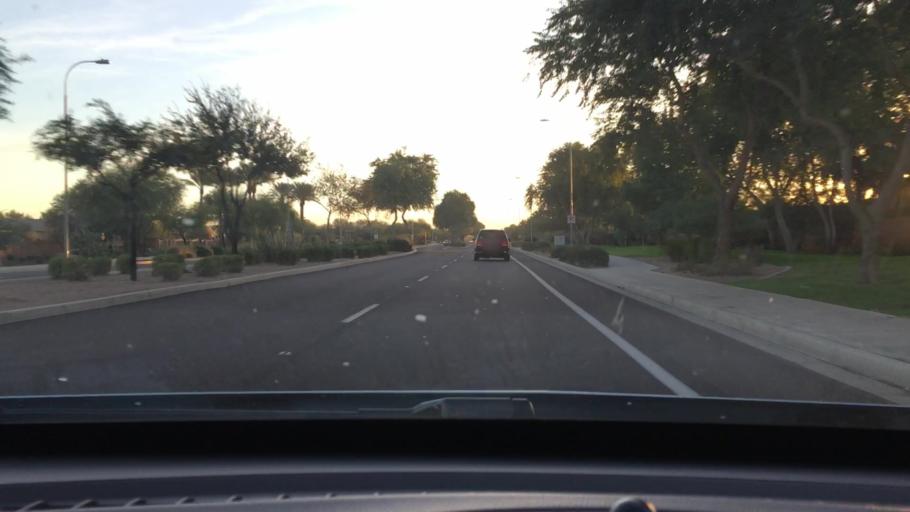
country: US
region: Arizona
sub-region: Maricopa County
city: Chandler
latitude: 33.2337
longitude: -111.7851
